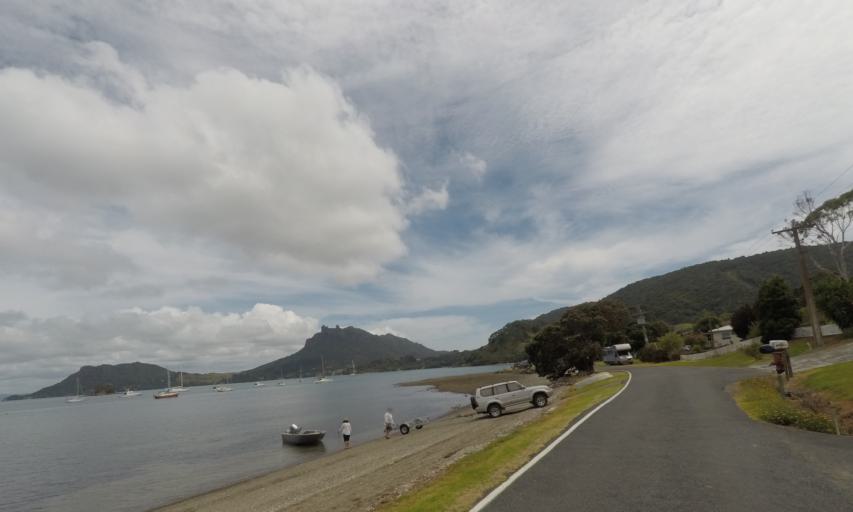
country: NZ
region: Northland
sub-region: Whangarei
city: Ruakaka
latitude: -35.8473
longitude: 174.5353
